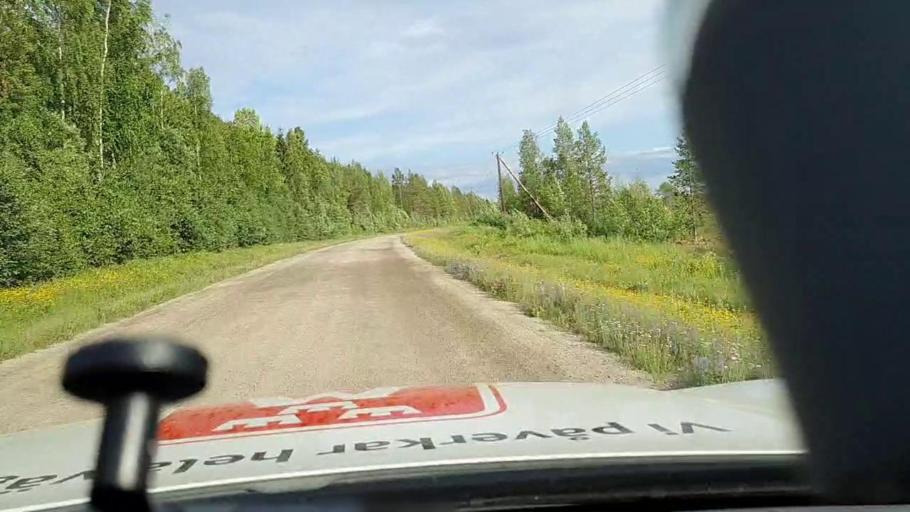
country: SE
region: Norrbotten
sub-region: Alvsbyns Kommun
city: AElvsbyn
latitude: 66.1809
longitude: 21.2264
